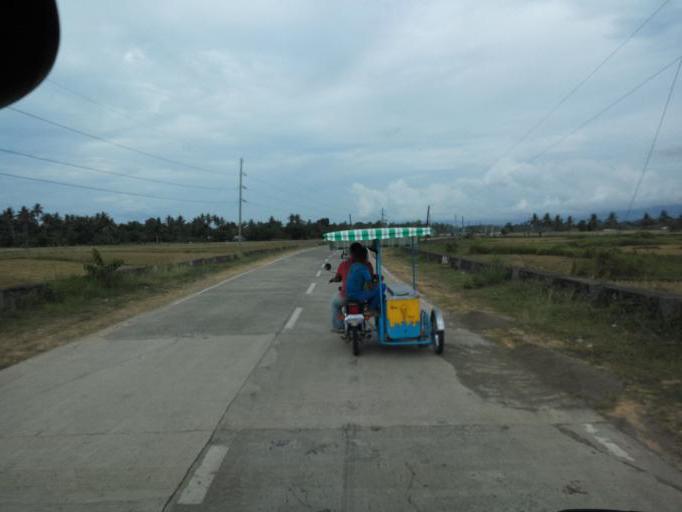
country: PH
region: Cagayan Valley
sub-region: Province of Cagayan
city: Santa Teresita
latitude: 18.2379
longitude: 121.9008
